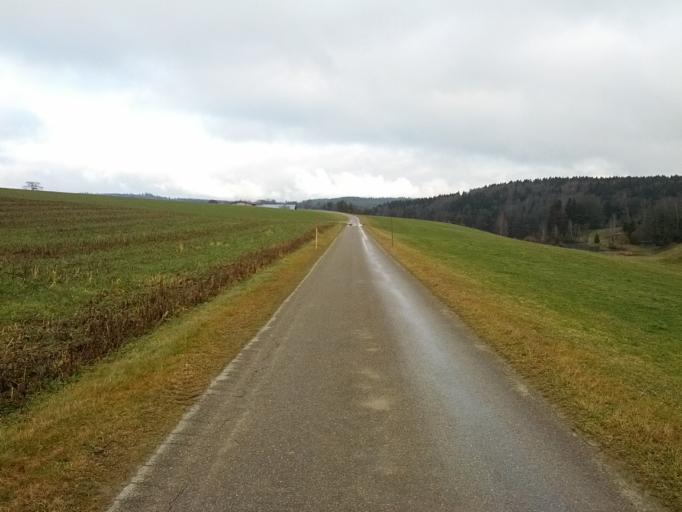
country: DE
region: Baden-Wuerttemberg
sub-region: Tuebingen Region
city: Steinhausen an der Rottum
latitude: 47.9824
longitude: 9.9689
